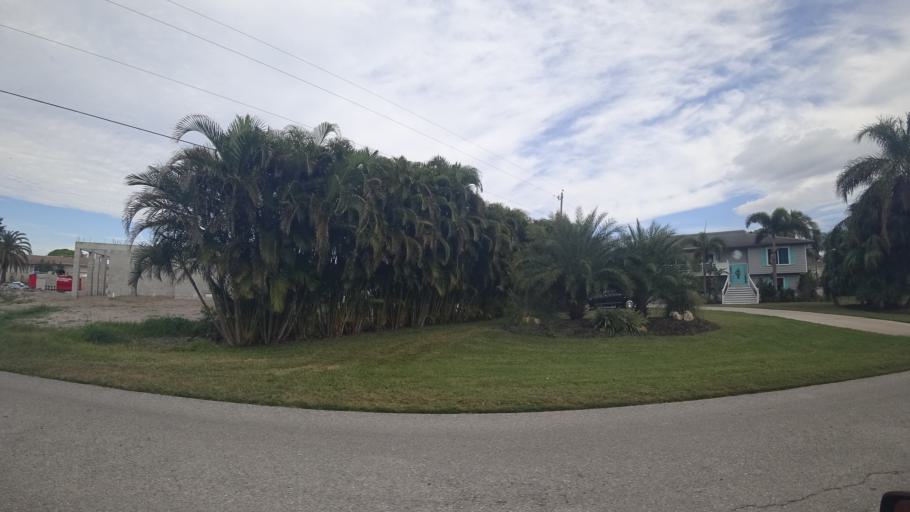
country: US
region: Florida
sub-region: Manatee County
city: West Bradenton
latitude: 27.4778
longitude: -82.6420
